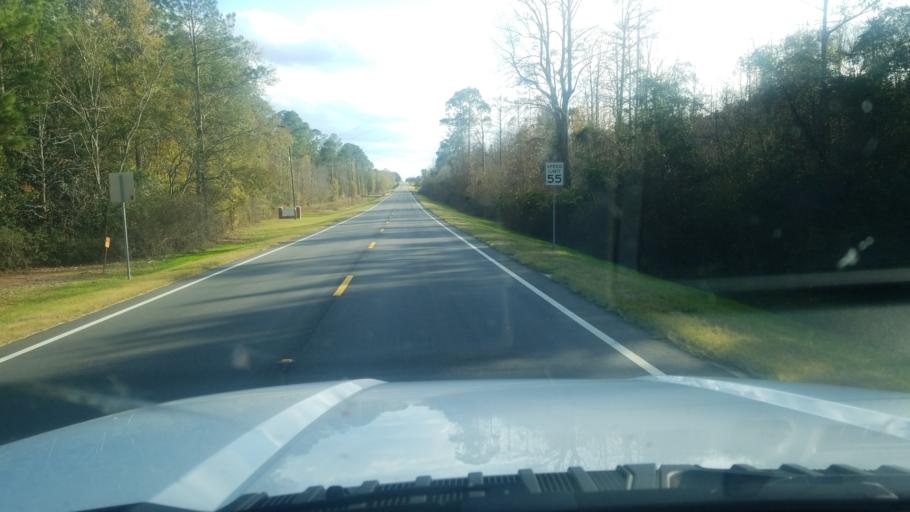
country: US
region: Georgia
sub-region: Candler County
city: Metter
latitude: 32.2751
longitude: -82.1373
